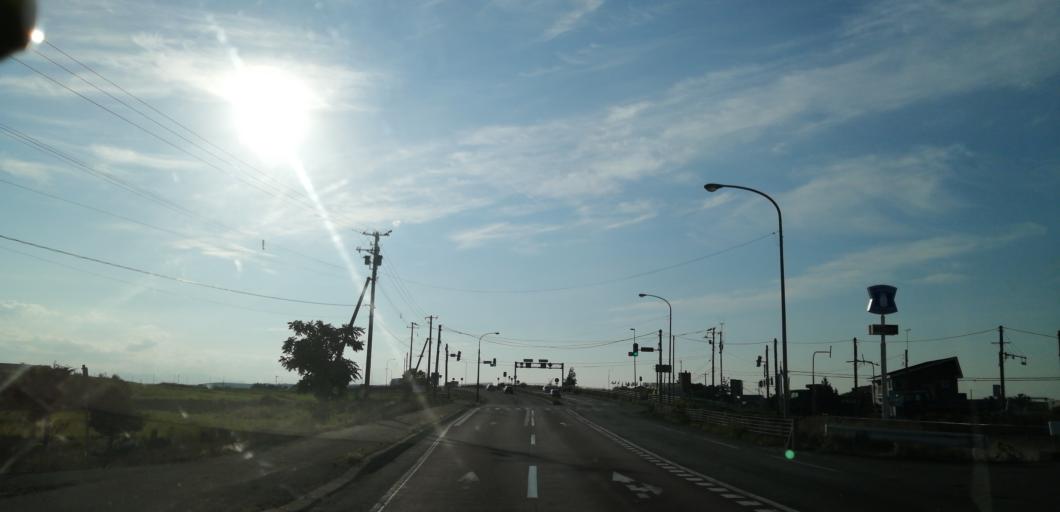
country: JP
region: Hokkaido
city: Kitahiroshima
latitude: 42.9965
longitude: 141.5900
